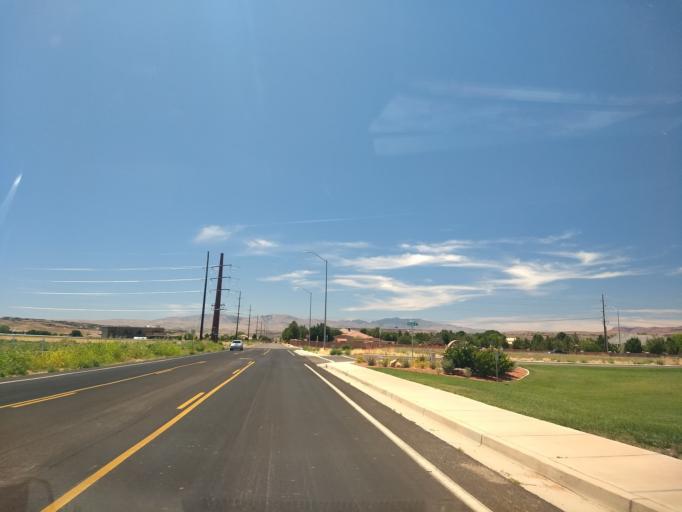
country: US
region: Utah
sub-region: Washington County
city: Washington
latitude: 37.0890
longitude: -113.4983
